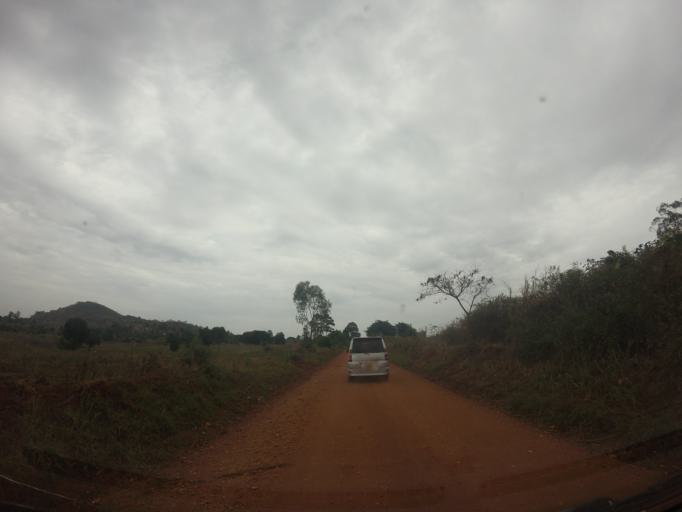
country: UG
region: Northern Region
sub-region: Arua District
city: Arua
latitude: 2.7995
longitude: 30.8757
